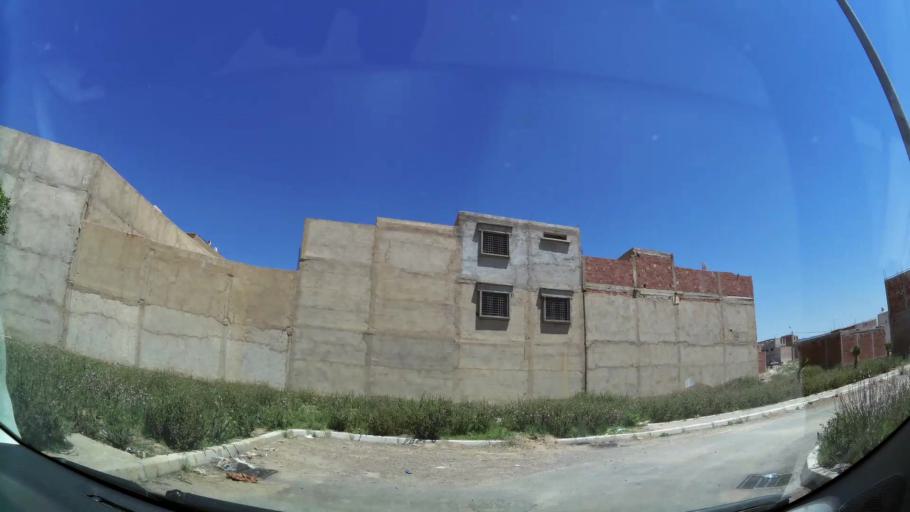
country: MA
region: Oriental
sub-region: Oujda-Angad
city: Oujda
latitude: 34.6749
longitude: -1.8638
